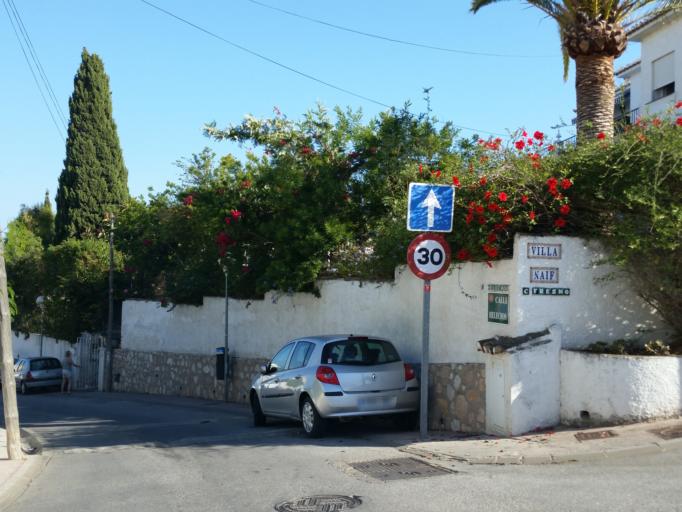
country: ES
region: Andalusia
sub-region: Provincia de Malaga
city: Fuengirola
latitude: 36.5659
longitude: -4.6085
